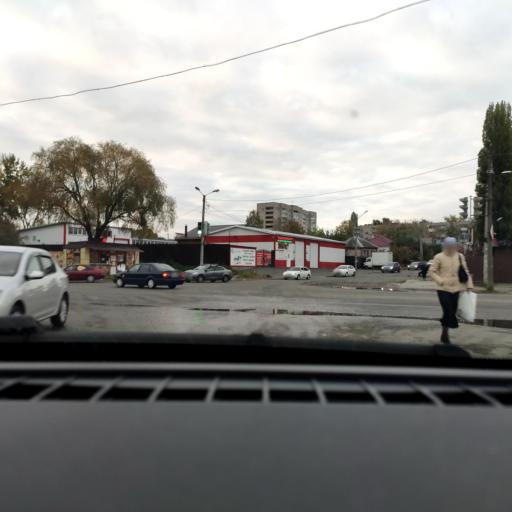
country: RU
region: Voronezj
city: Maslovka
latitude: 51.6222
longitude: 39.2522
